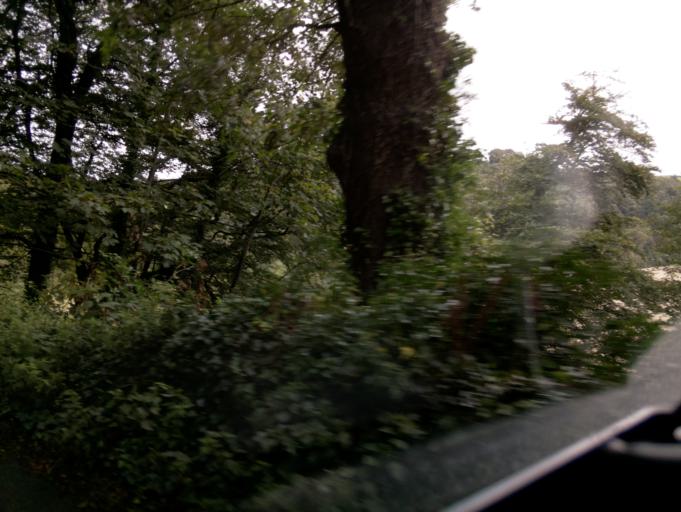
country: GB
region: England
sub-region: Devon
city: Dartmouth
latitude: 50.3172
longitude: -3.6139
